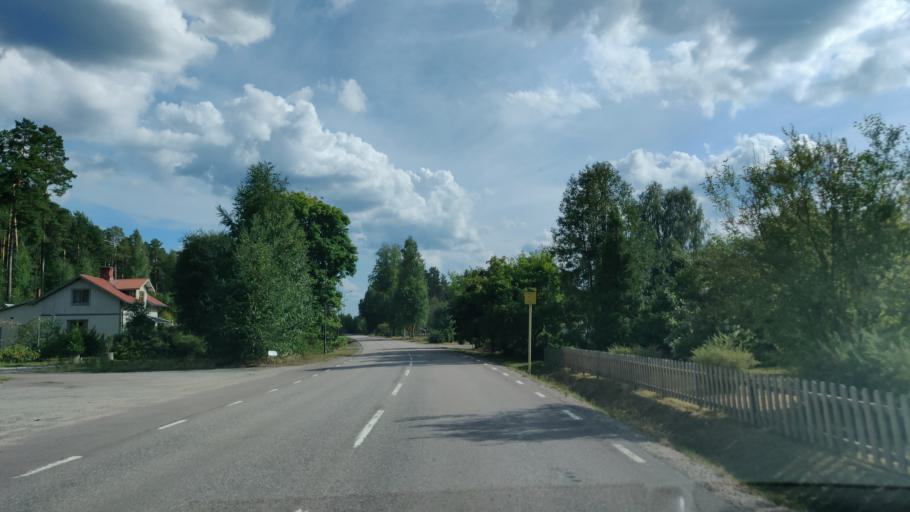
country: SE
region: Vaermland
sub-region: Hagfors Kommun
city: Ekshaerad
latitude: 60.1167
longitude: 13.5628
